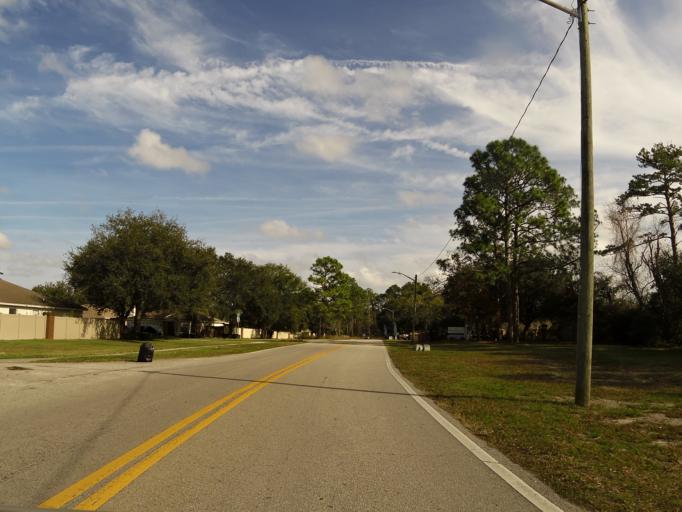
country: US
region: Florida
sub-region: Duval County
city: Jacksonville
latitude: 30.3310
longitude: -81.5434
